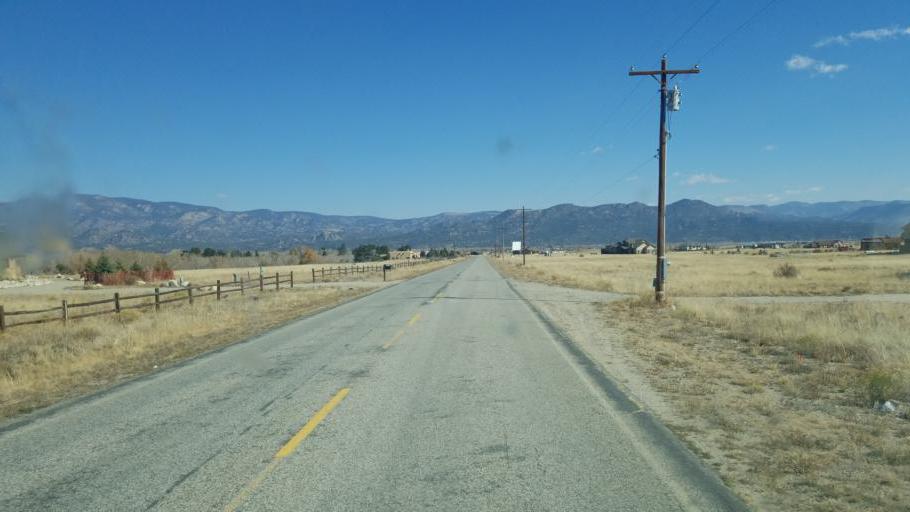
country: US
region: Colorado
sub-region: Chaffee County
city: Buena Vista
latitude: 38.8183
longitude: -106.1936
